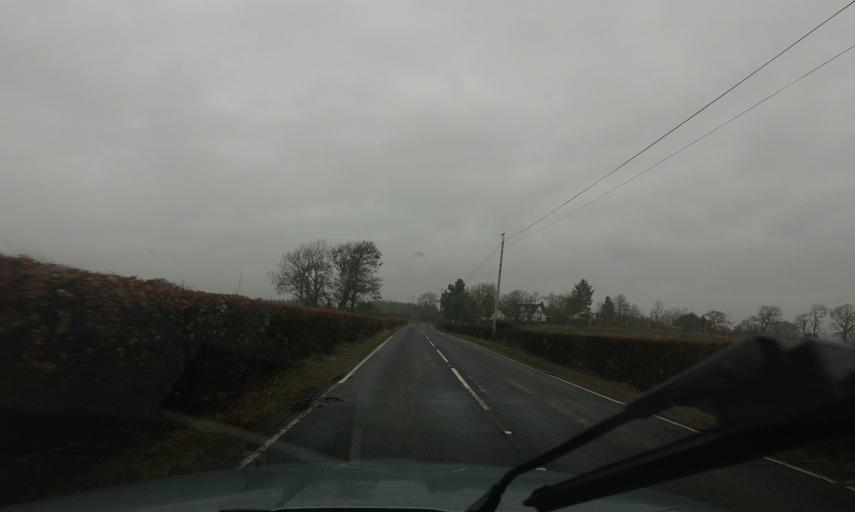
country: GB
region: Scotland
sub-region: Stirling
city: Balfron
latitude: 56.1093
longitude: -4.3582
